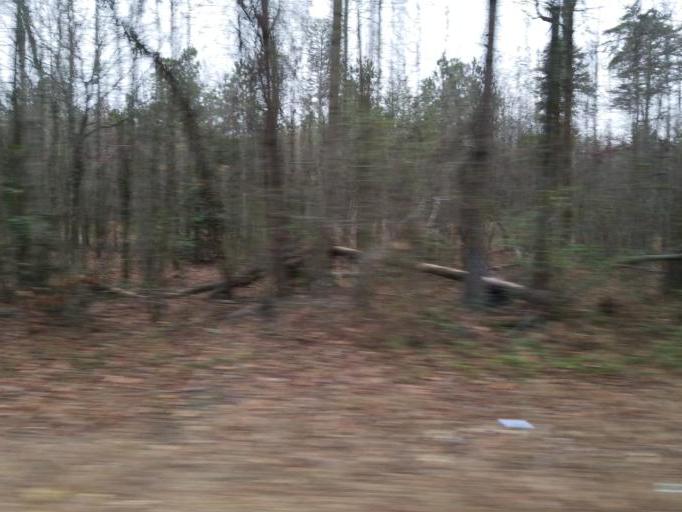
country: US
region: Georgia
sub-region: Dawson County
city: Dawsonville
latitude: 34.4688
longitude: -84.1486
